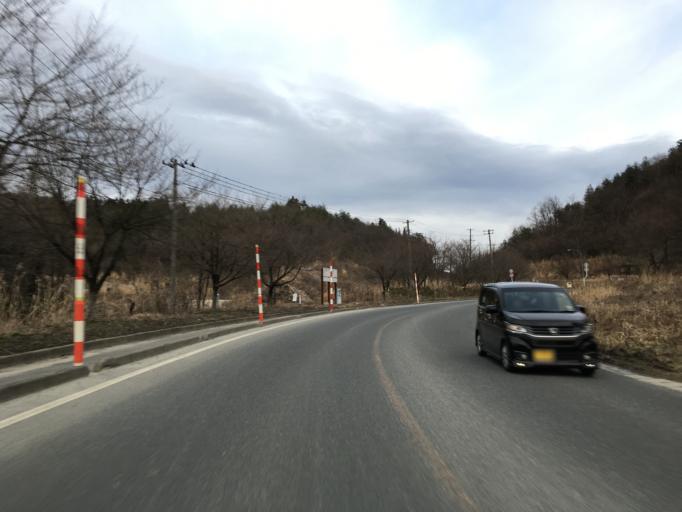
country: JP
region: Yamagata
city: Nagai
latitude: 38.0970
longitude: 140.0561
